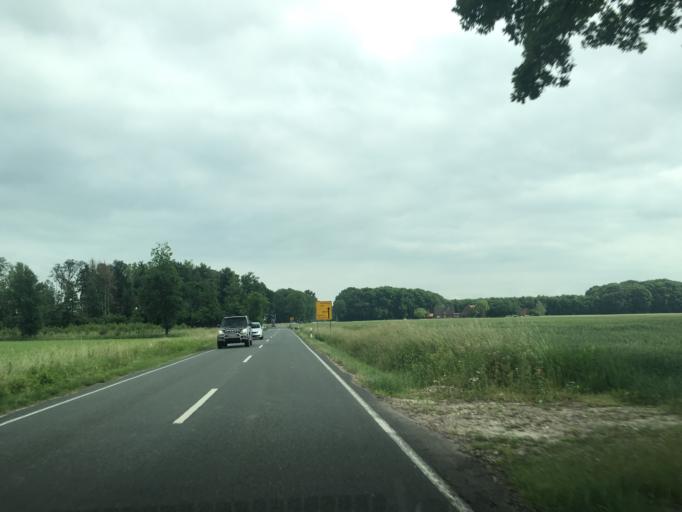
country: DE
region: North Rhine-Westphalia
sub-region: Regierungsbezirk Munster
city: Horstmar
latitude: 52.1022
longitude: 7.3436
